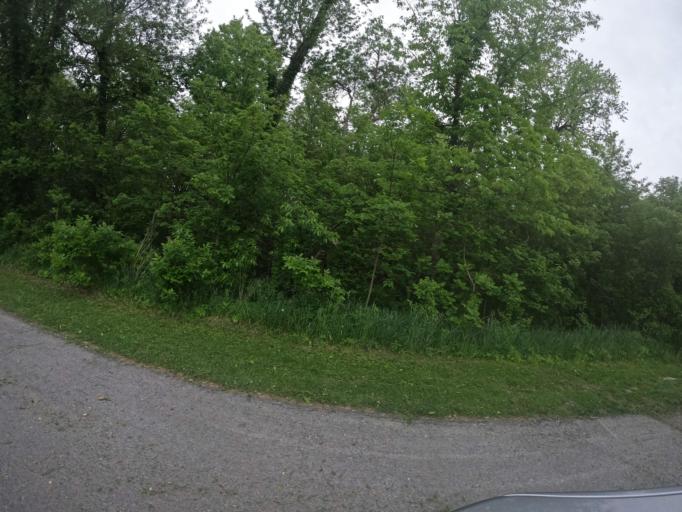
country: US
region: Nebraska
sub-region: Sarpy County
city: Offutt Air Force Base
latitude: 41.0508
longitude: -95.9627
